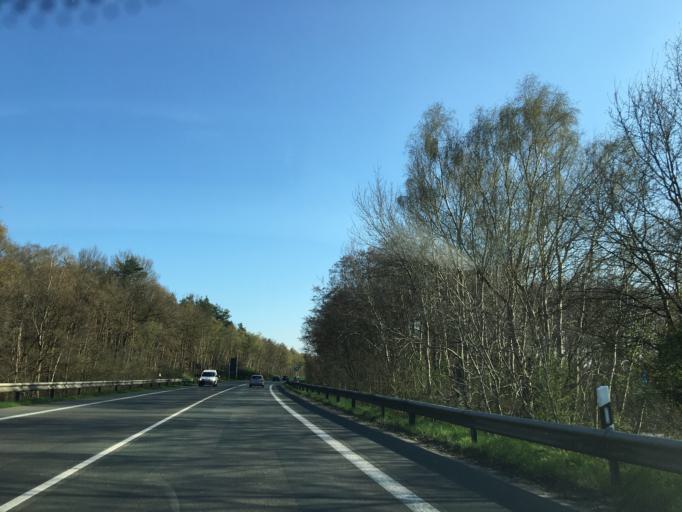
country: DE
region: North Rhine-Westphalia
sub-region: Regierungsbezirk Munster
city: Greven
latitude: 52.0562
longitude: 7.6786
